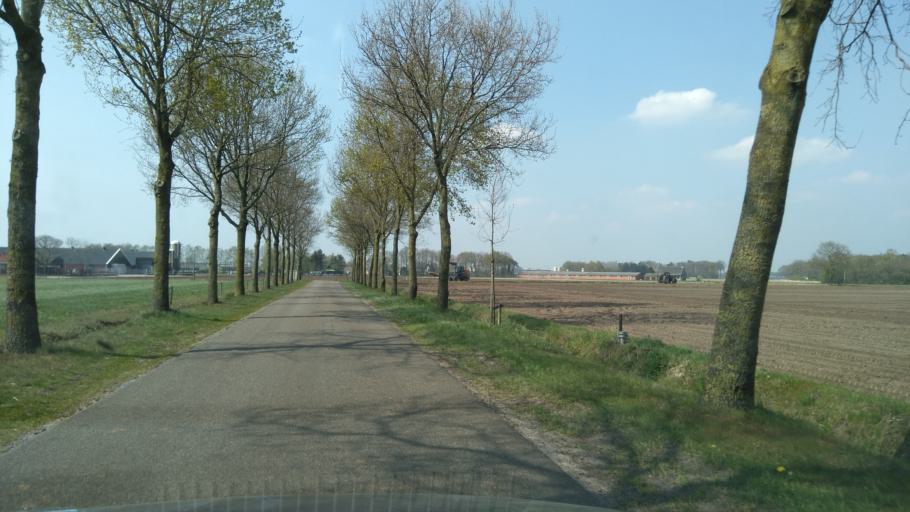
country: NL
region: North Brabant
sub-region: Gemeente Baarle-Nassau
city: Baarle-Nassau
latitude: 51.4281
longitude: 4.9093
